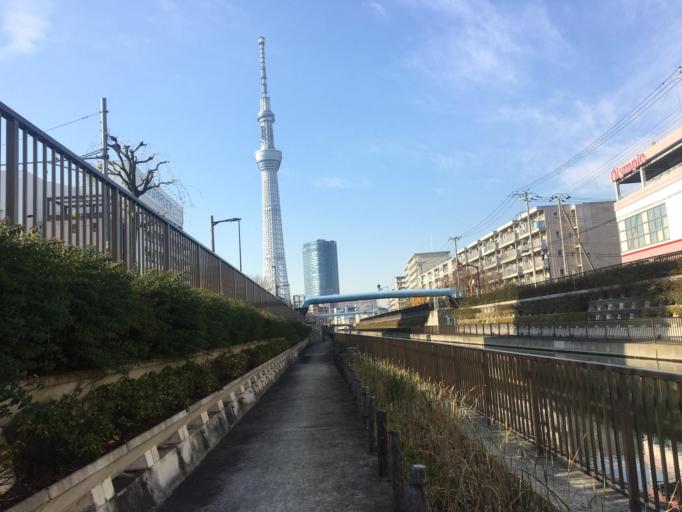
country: JP
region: Tokyo
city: Urayasu
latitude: 35.7063
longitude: 139.8230
